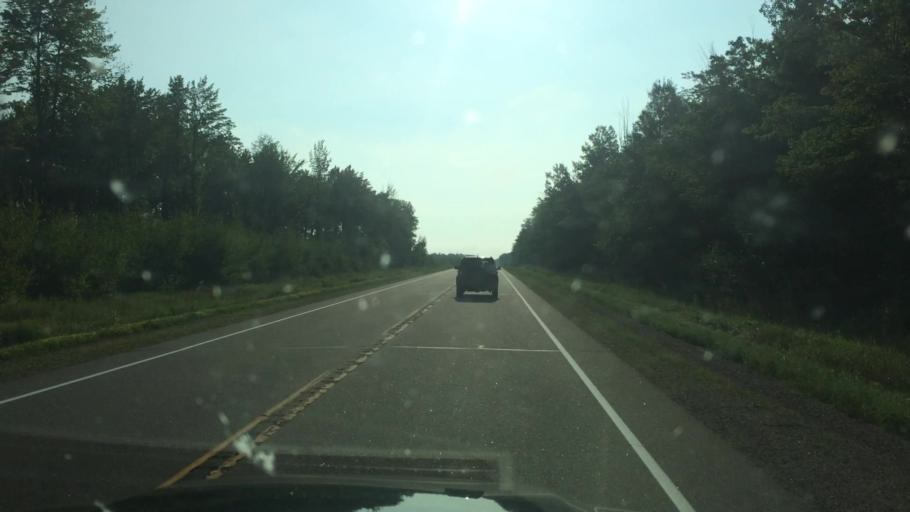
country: US
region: Wisconsin
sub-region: Langlade County
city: Antigo
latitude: 45.1469
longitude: -89.3778
